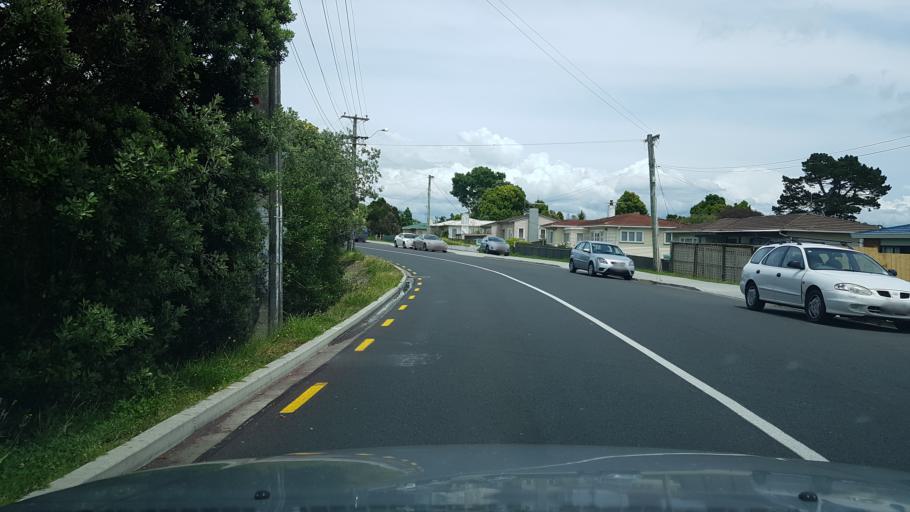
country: NZ
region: Auckland
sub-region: Auckland
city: North Shore
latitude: -36.7990
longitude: 174.7503
